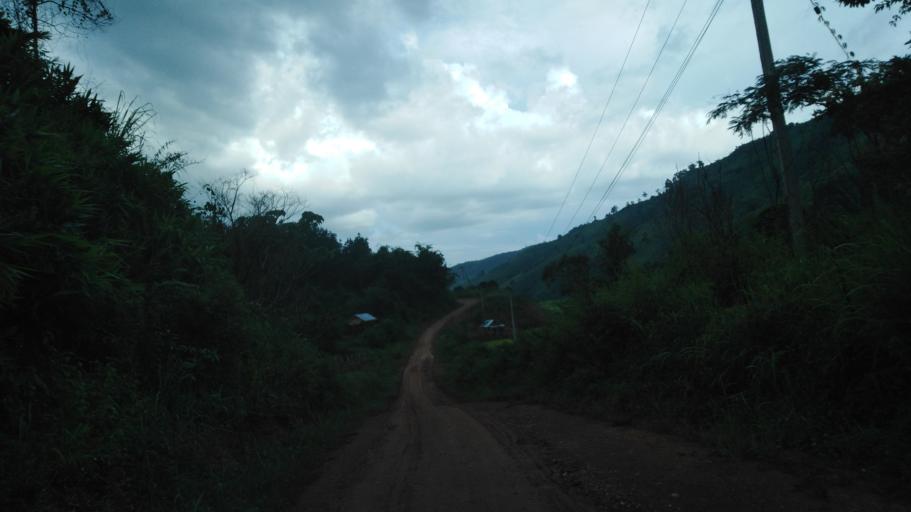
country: TH
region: Nan
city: Song Khwae
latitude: 19.7423
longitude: 100.7107
